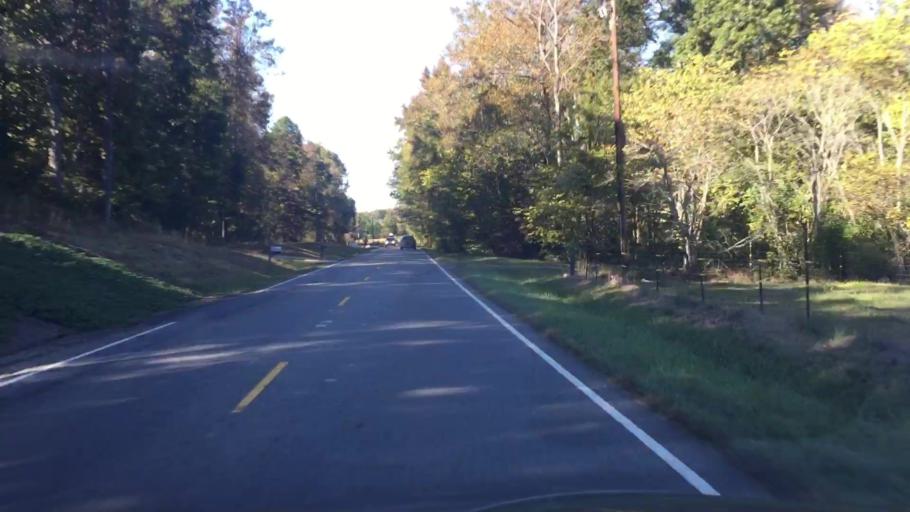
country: US
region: North Carolina
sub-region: Gaston County
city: Davidson
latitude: 35.5137
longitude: -80.7695
